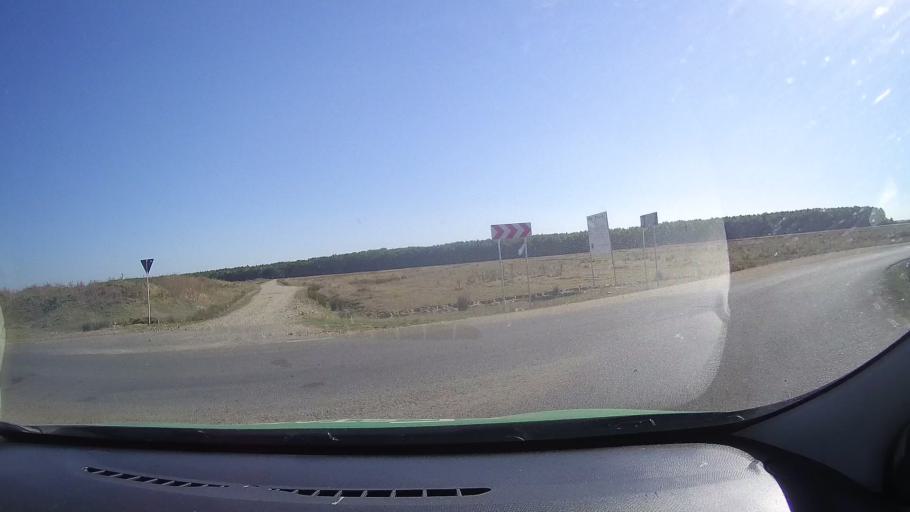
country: RO
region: Satu Mare
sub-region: Municipiul Satu Mare
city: Satmarel
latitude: 47.7032
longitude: 22.7765
